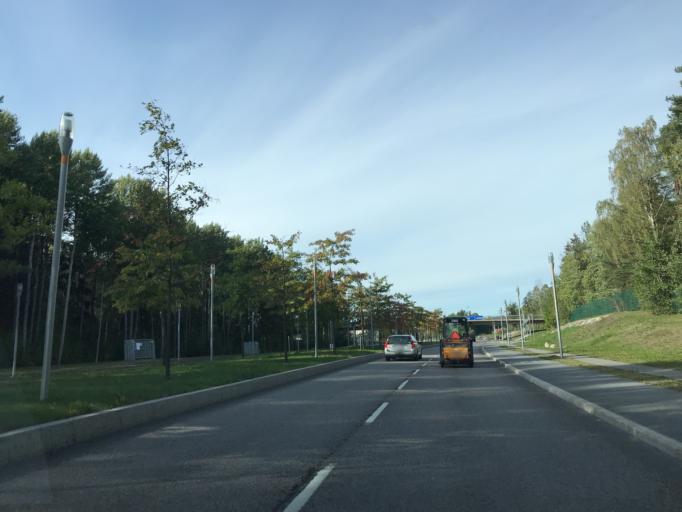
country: SE
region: Stockholm
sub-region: Stockholms Kommun
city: Kista
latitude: 59.4108
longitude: 17.9339
